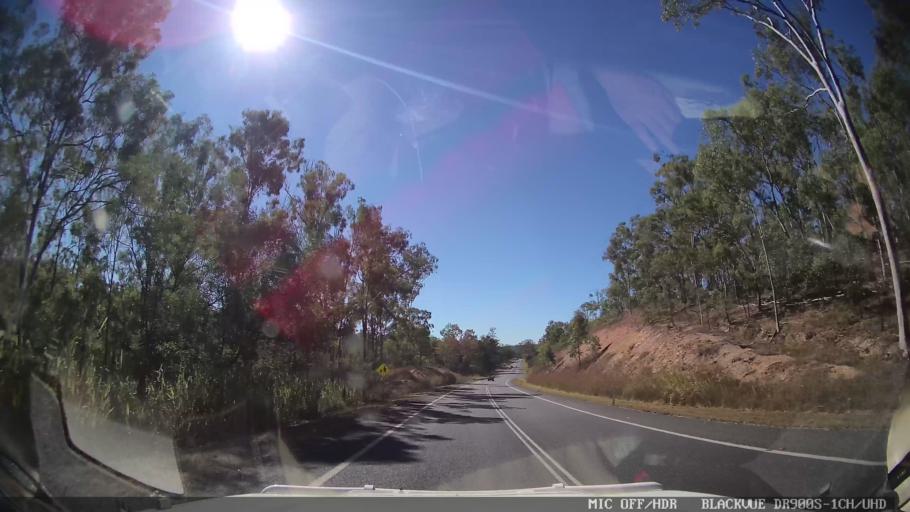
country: AU
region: Queensland
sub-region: Gladstone
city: Toolooa
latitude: -23.9631
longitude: 151.2176
